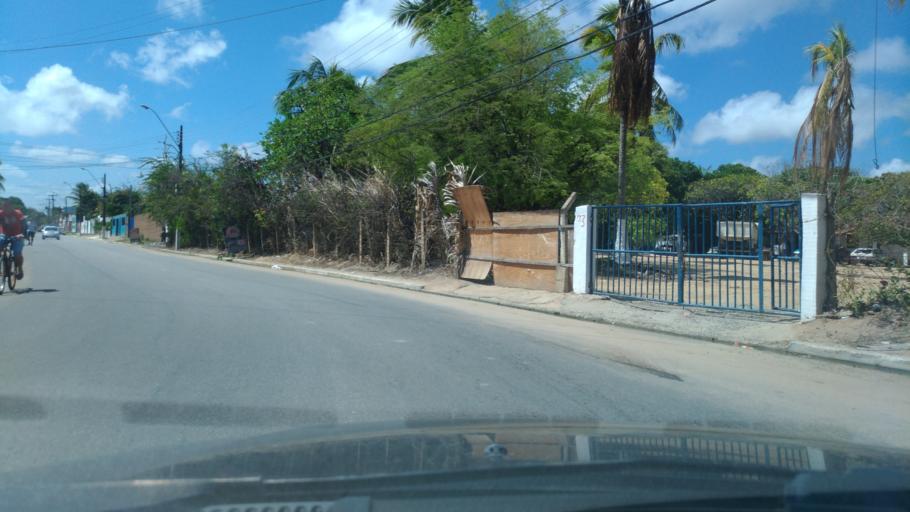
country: BR
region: Alagoas
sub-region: Maceio
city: Maceio
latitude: -9.6218
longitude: -35.7080
